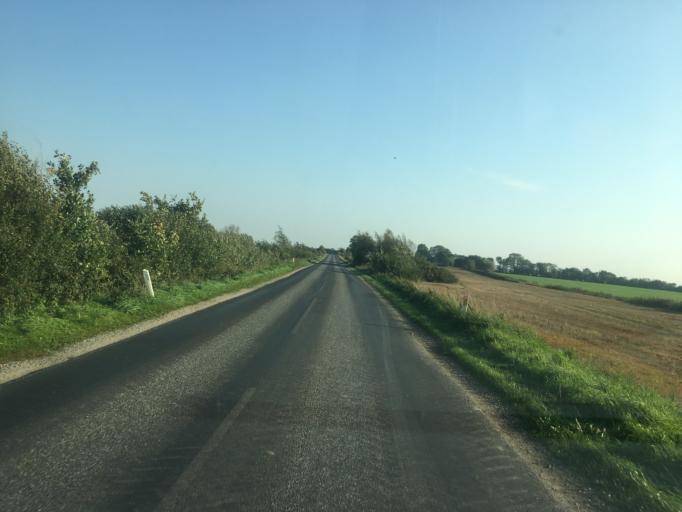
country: DE
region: Schleswig-Holstein
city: Bramstedtlund
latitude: 54.9545
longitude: 9.0545
